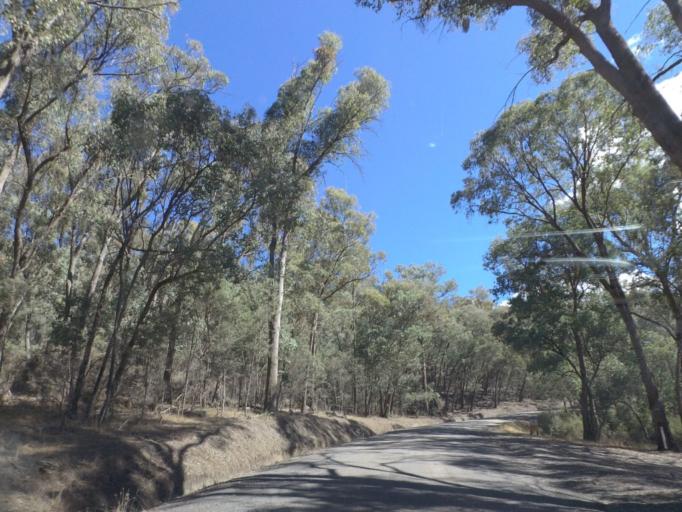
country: AU
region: Victoria
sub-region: Murrindindi
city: Alexandra
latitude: -37.3154
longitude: 145.8172
